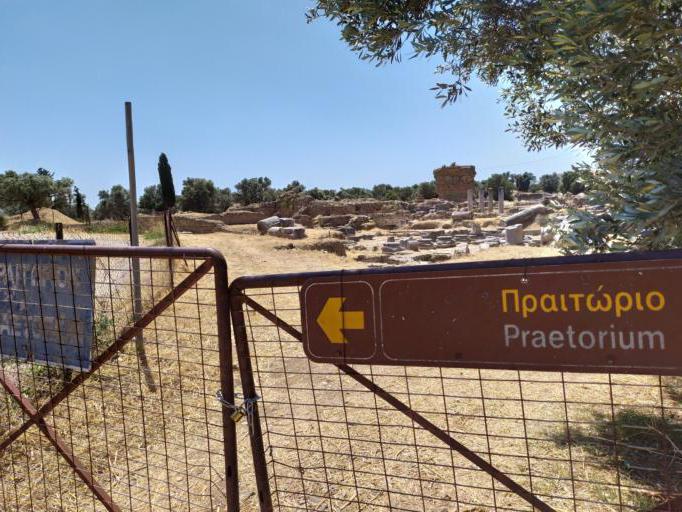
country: GR
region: Crete
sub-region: Nomos Irakleiou
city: Agioi Deka
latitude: 35.0588
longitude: 24.9522
